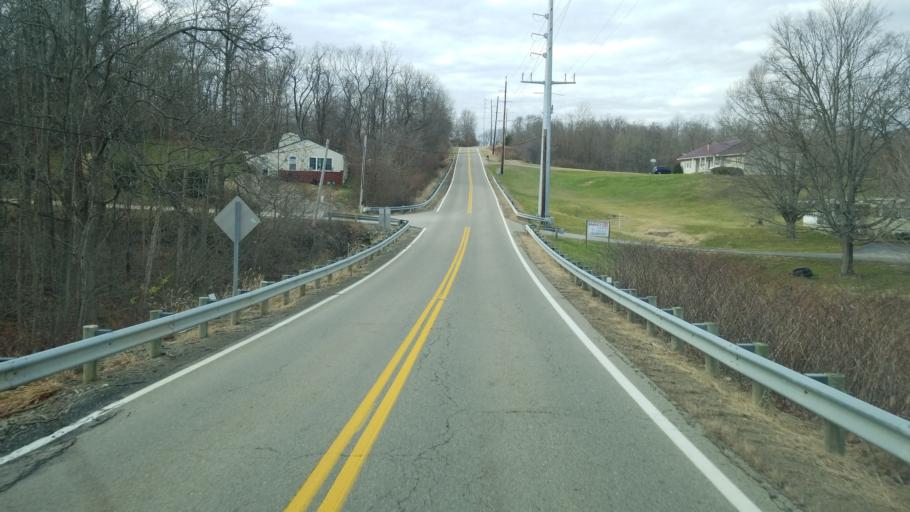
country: US
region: Ohio
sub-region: Ross County
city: Frankfort
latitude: 39.3466
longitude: -83.1816
